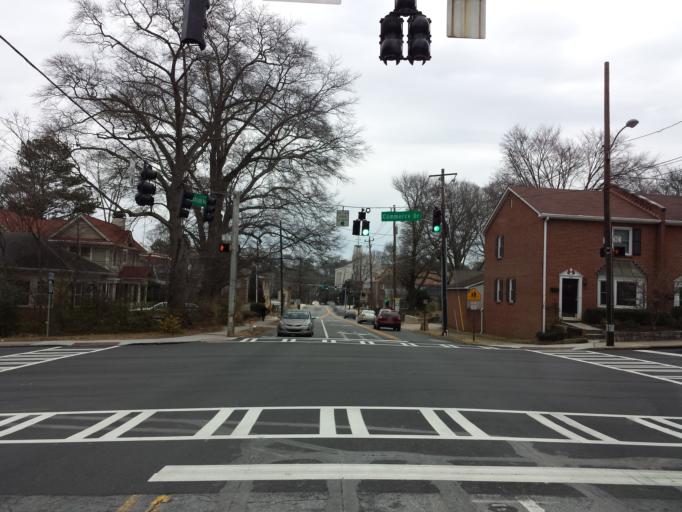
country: US
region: Georgia
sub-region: DeKalb County
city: Decatur
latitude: 33.7756
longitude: -84.2922
